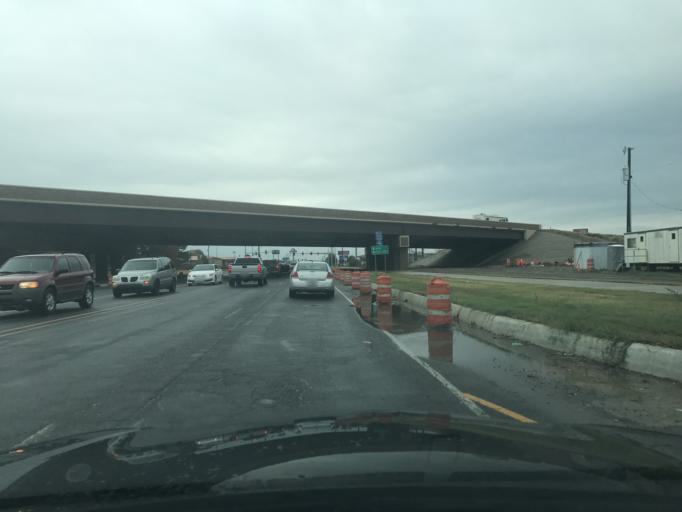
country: US
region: Arkansas
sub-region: Faulkner County
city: Conway
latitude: 35.0915
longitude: -92.4237
